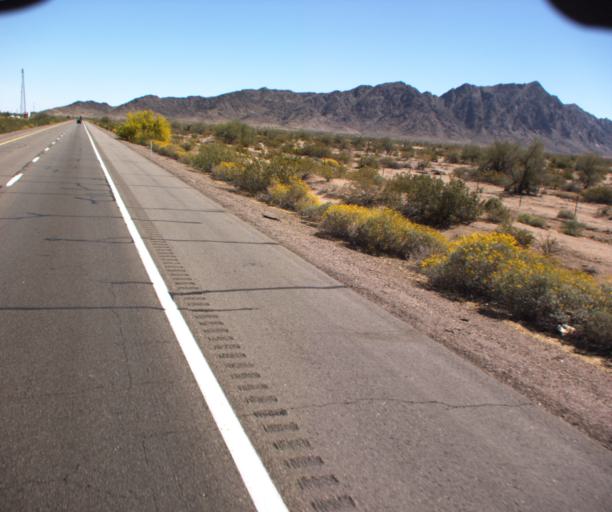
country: US
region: Arizona
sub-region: Yuma County
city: Wellton
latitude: 32.7203
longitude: -113.7760
